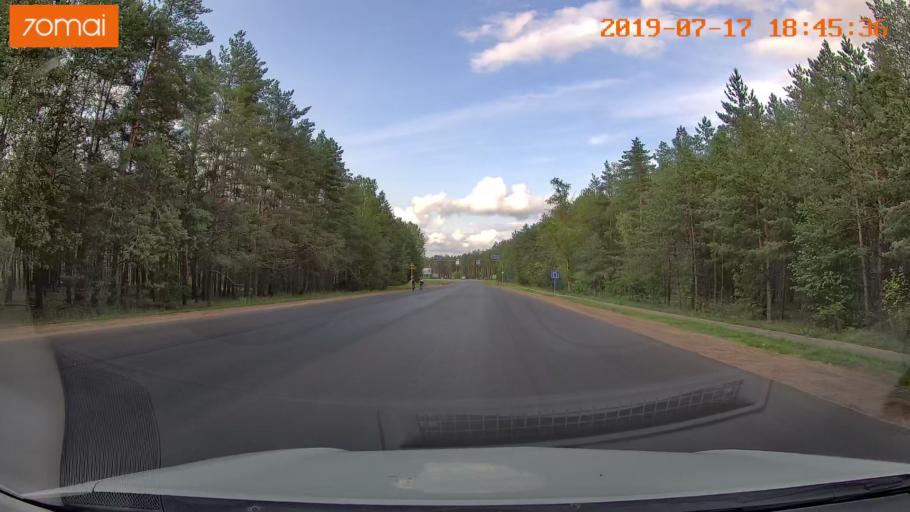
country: BY
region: Mogilev
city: Asipovichy
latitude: 53.3261
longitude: 28.6566
